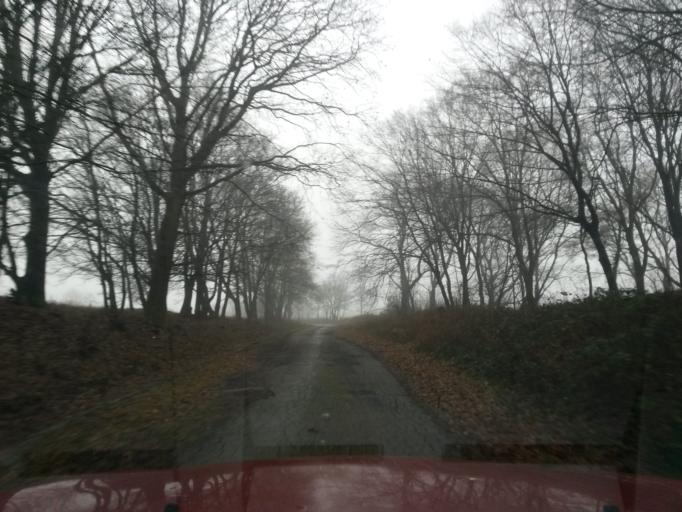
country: SK
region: Presovsky
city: Vranov nad Topl'ou
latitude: 48.8855
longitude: 21.7551
